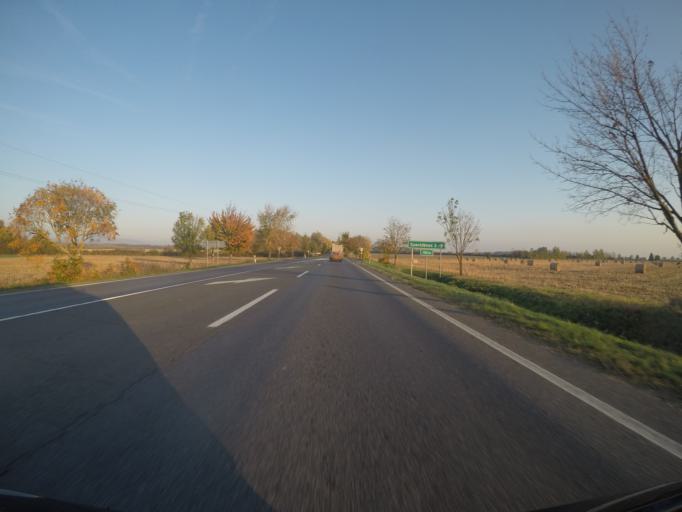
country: HU
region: Baranya
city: Szentlorinc
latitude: 46.0408
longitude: 17.9257
